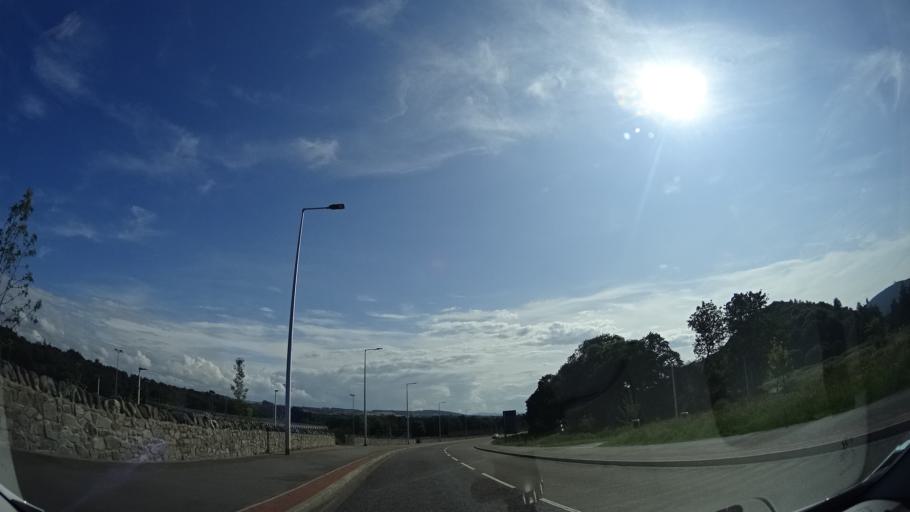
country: GB
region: Scotland
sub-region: Highland
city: Inverness
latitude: 57.4630
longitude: -4.2425
